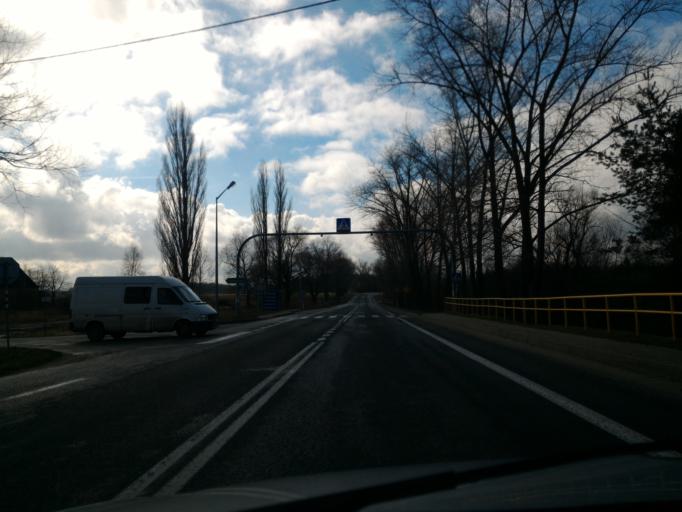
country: PL
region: Lower Silesian Voivodeship
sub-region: Powiat zgorzelecki
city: Sulikow
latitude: 51.0677
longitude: 15.0057
